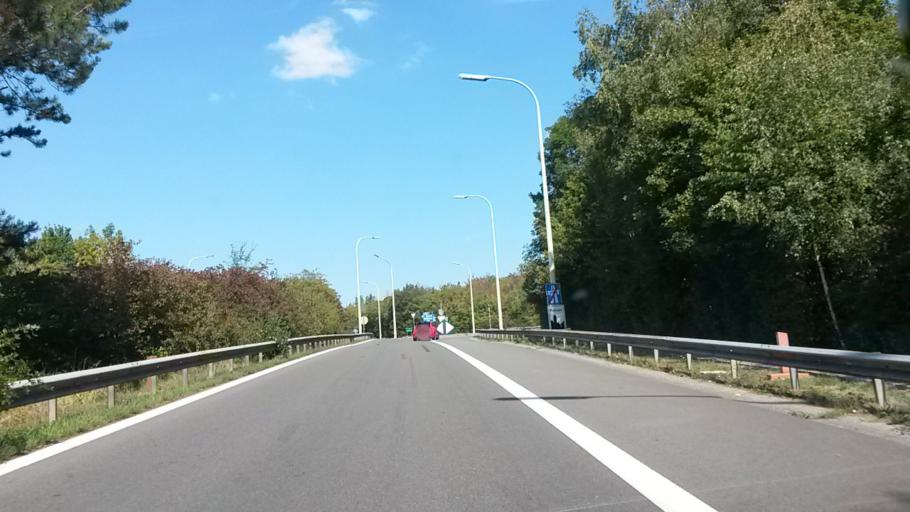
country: BE
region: Wallonia
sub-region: Province du Hainaut
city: Farciennes
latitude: 50.4392
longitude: 4.4986
